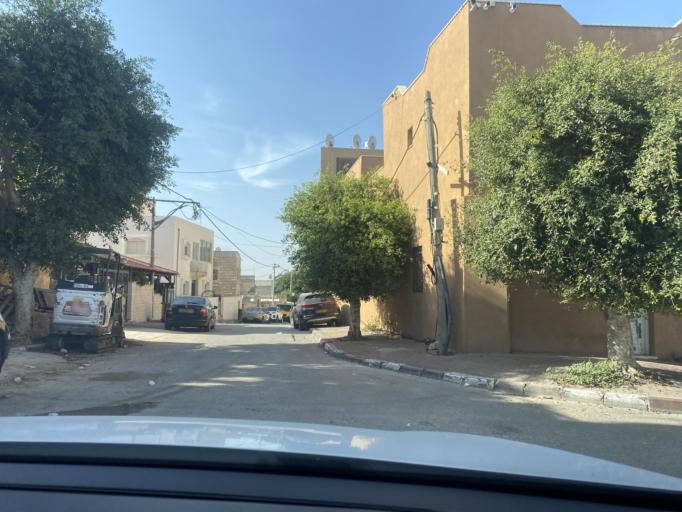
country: IL
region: Central District
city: Kafr Qasim
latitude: 32.1304
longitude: 34.9731
